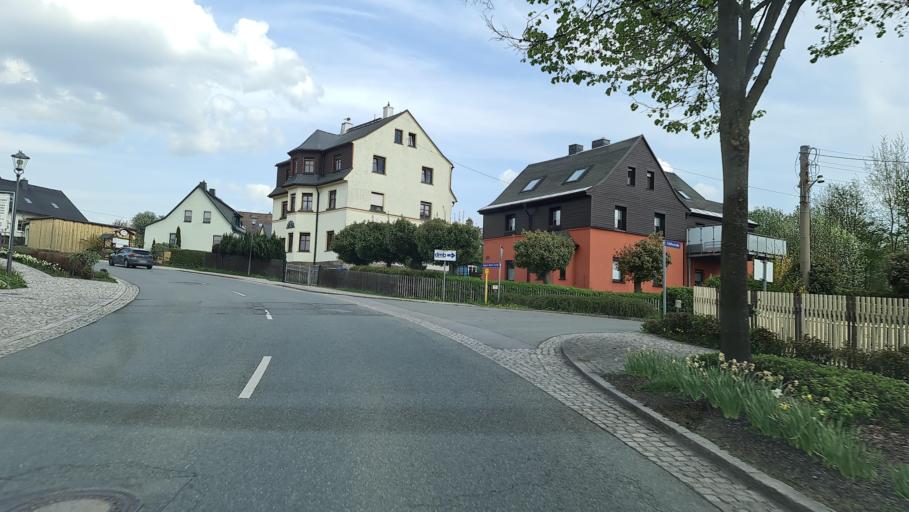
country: DE
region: Saxony
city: Beierfeld
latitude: 50.5672
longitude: 12.7953
